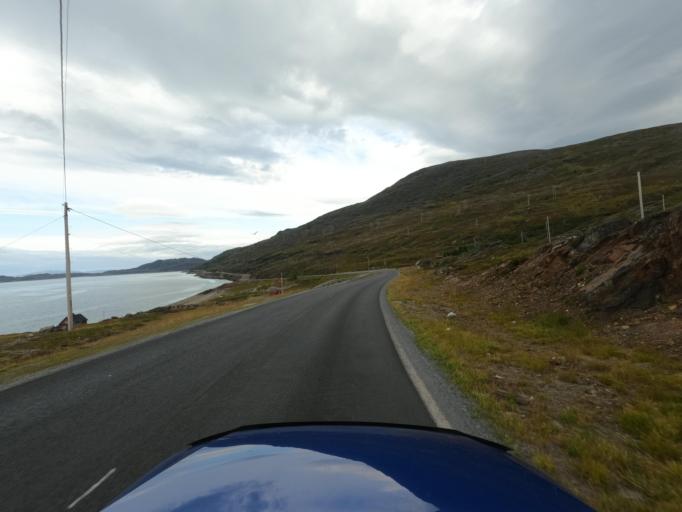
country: NO
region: Finnmark Fylke
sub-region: Hammerfest
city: Rypefjord
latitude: 70.5645
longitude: 23.6979
